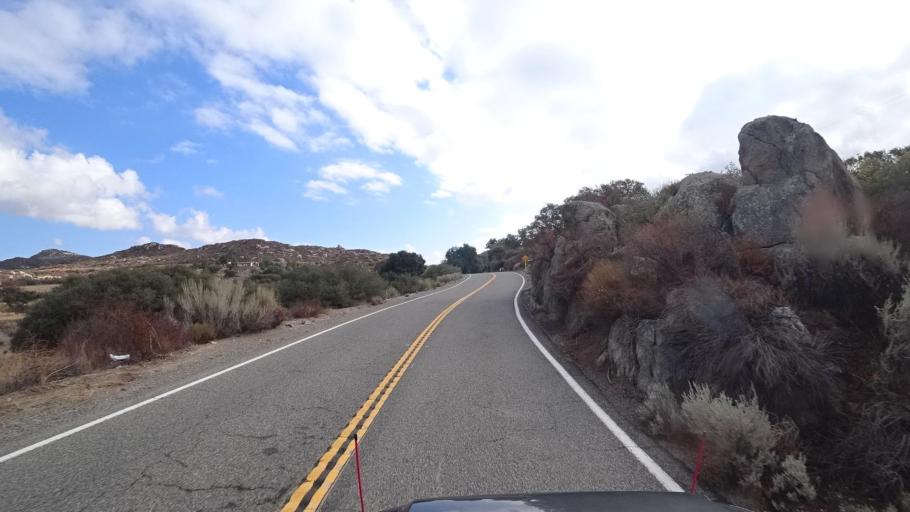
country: US
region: California
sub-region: San Diego County
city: Campo
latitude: 32.5984
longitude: -116.4988
